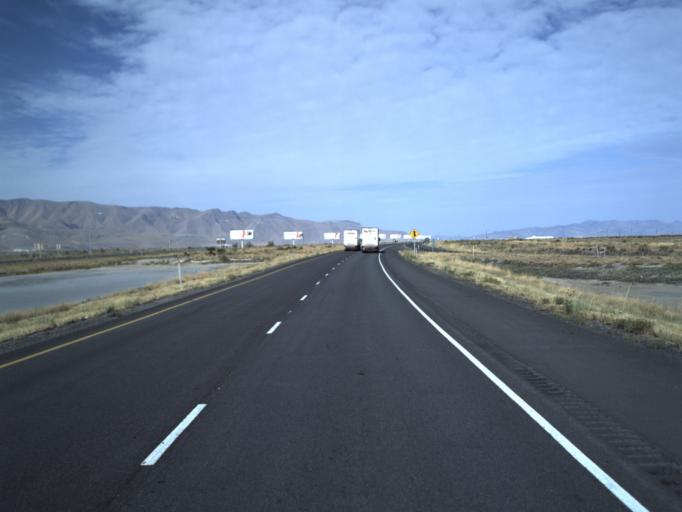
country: US
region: Utah
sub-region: Tooele County
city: Grantsville
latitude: 40.6856
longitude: -112.4462
